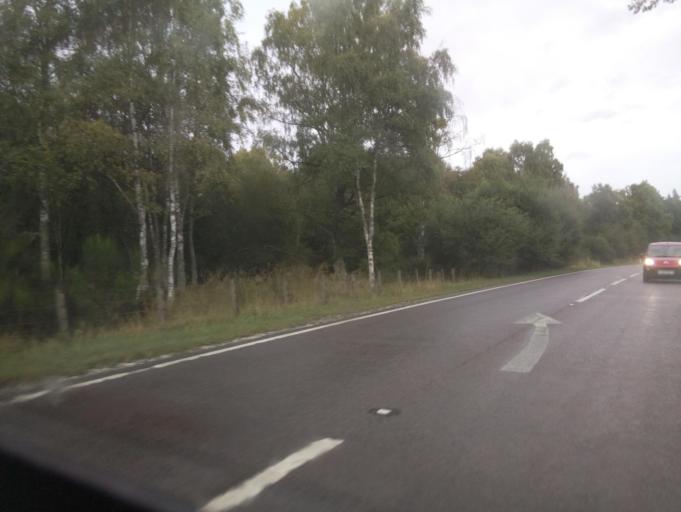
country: GB
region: Scotland
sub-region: Highland
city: Aviemore
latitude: 57.2595
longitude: -3.7491
